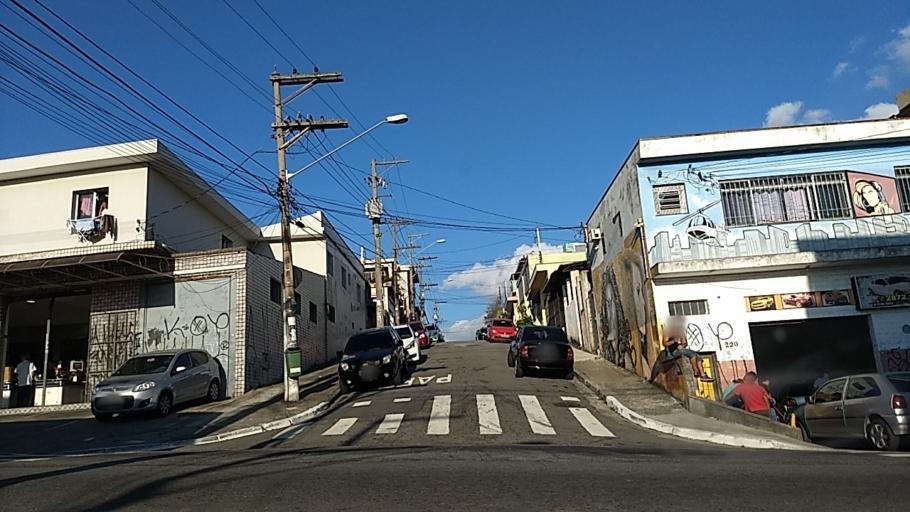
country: BR
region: Sao Paulo
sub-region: Sao Paulo
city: Sao Paulo
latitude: -23.4970
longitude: -46.5940
